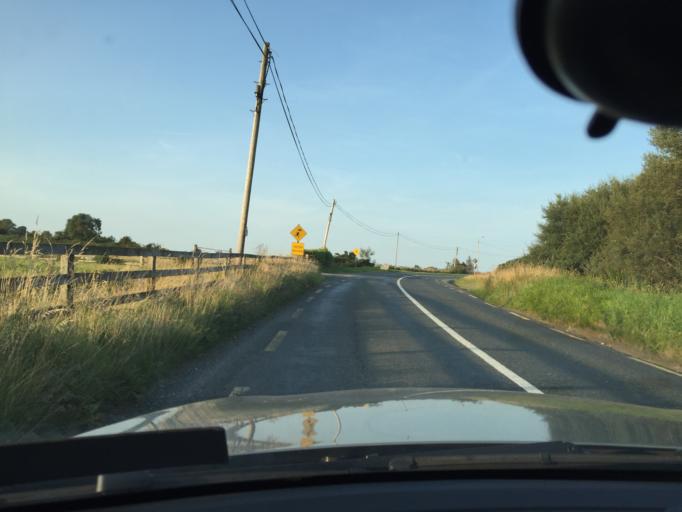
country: IE
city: Newtownmountkennedy
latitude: 53.0594
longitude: -6.2338
